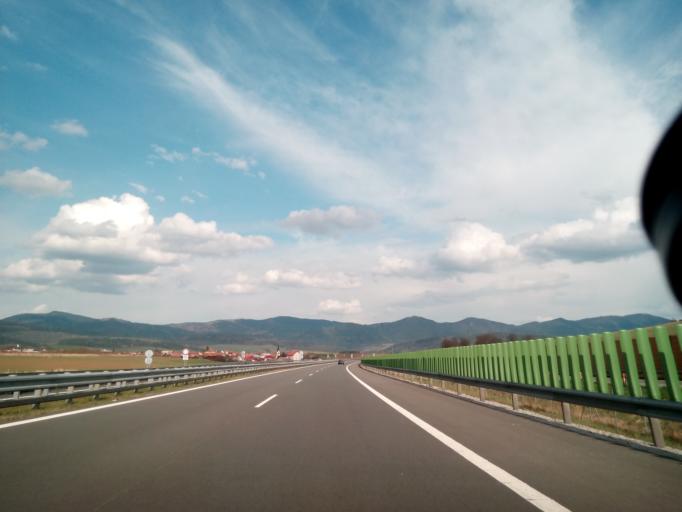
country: SK
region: Presovsky
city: Spisske Podhradie
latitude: 49.0080
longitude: 20.7563
